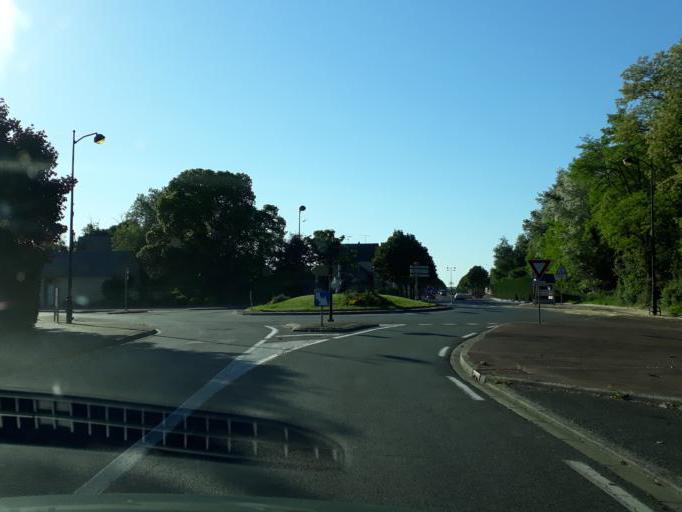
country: FR
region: Centre
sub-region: Departement du Loiret
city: Briare
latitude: 47.6306
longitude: 2.7483
